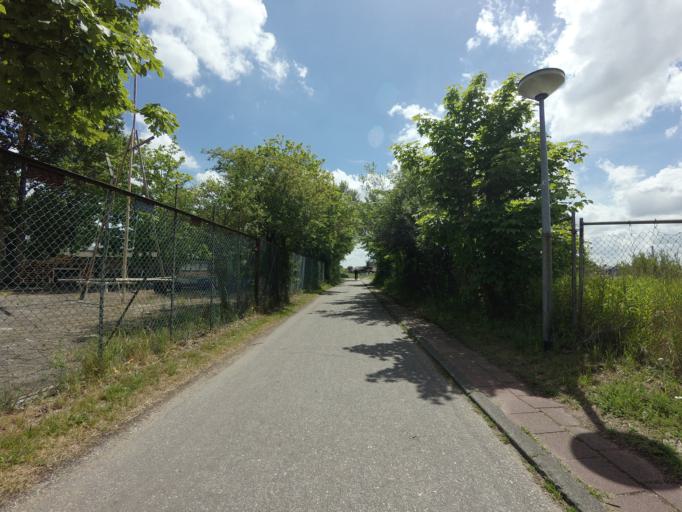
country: NL
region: North Holland
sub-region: Gemeente Zaanstad
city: Zaanstad
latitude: 52.4794
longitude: 4.8133
